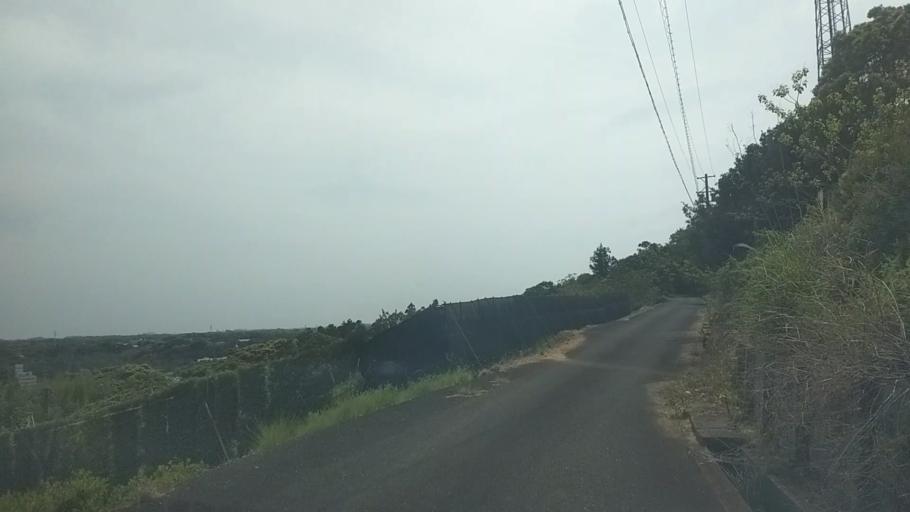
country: JP
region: Shizuoka
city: Kosai-shi
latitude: 34.7710
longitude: 137.6249
